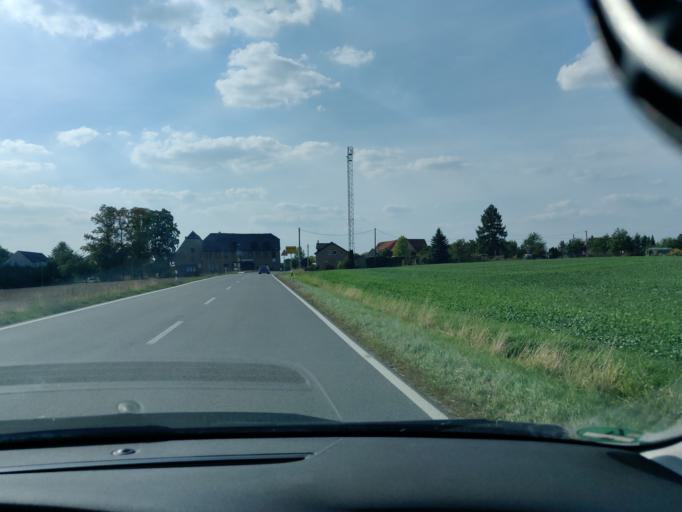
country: DE
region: Saxony
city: Erlau
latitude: 51.0147
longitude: 12.8808
